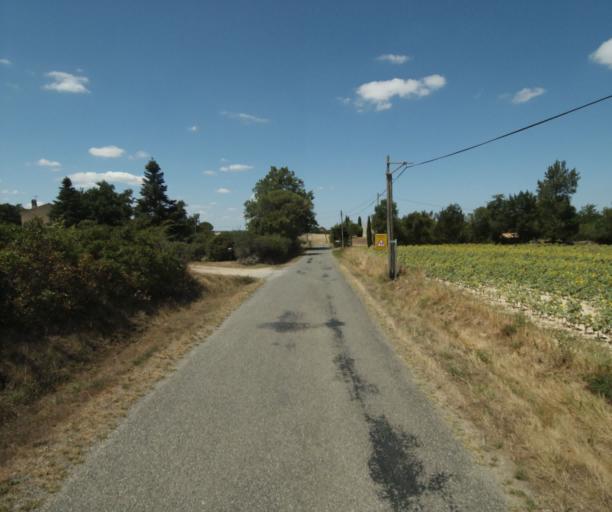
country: FR
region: Midi-Pyrenees
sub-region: Departement de la Haute-Garonne
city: Saint-Felix-Lauragais
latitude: 43.4759
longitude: 1.8586
